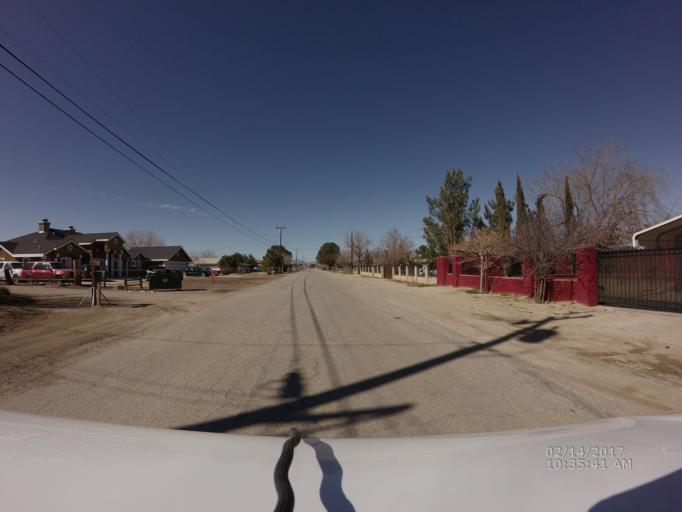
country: US
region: California
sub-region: Los Angeles County
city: Littlerock
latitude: 34.5616
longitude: -117.9483
